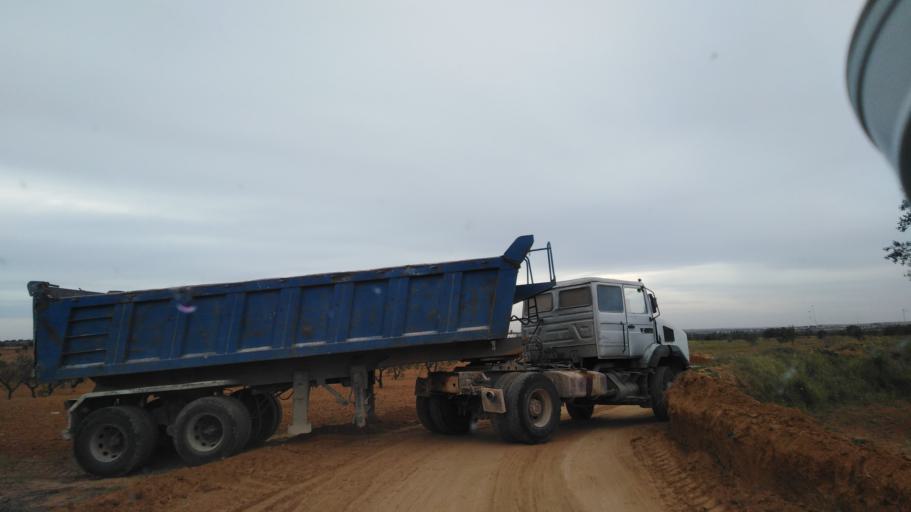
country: TN
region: Safaqis
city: Bi'r `Ali Bin Khalifah
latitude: 34.7696
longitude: 10.3747
